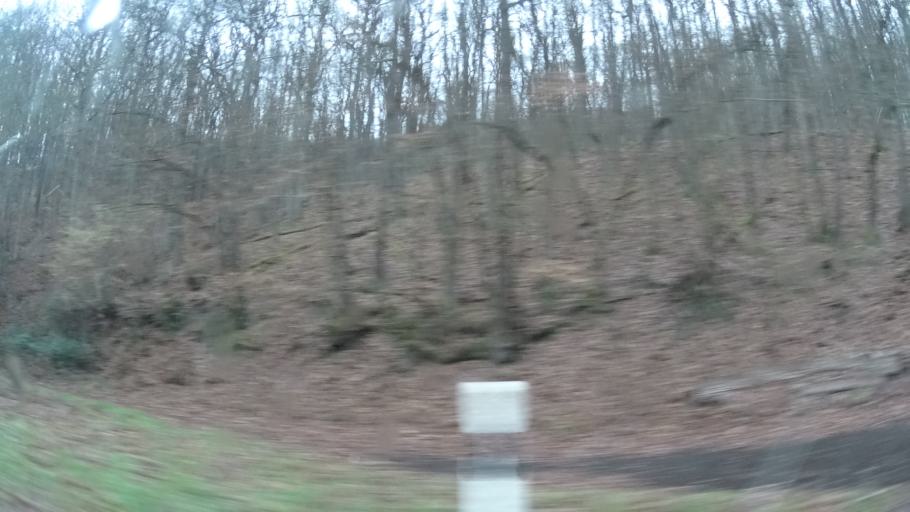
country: DE
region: Rheinland-Pfalz
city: Rockenhausen
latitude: 49.6228
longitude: 7.8434
